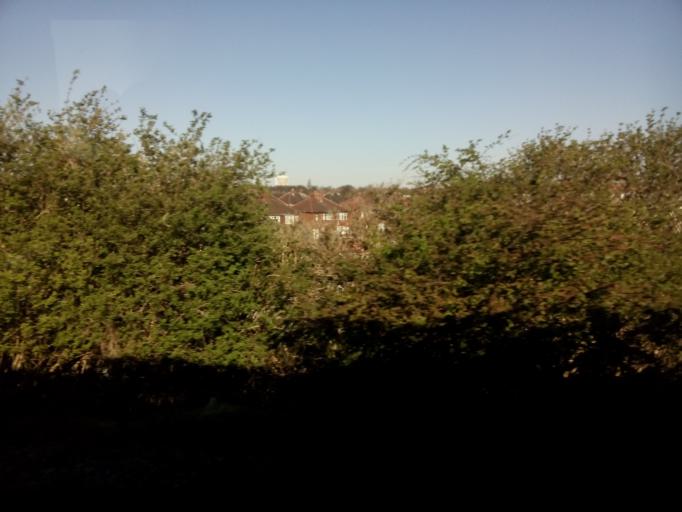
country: GB
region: England
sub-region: Borough of North Tyneside
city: Wallsend
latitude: 54.9918
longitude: -1.5629
